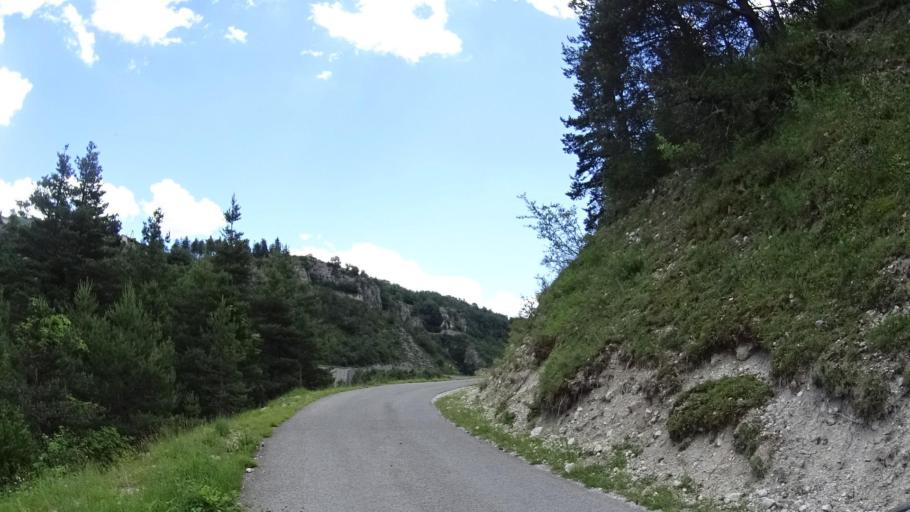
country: FR
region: Provence-Alpes-Cote d'Azur
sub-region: Departement des Alpes-de-Haute-Provence
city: Annot
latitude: 44.0198
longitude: 6.6283
